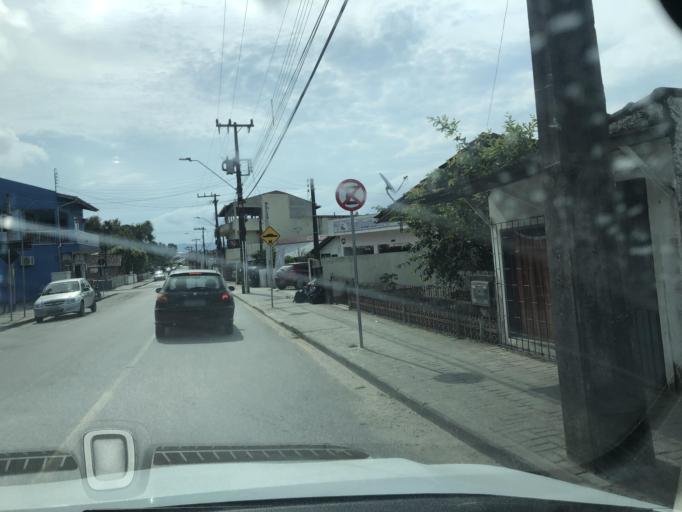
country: BR
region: Santa Catarina
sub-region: Sao Francisco Do Sul
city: Sao Francisco do Sul
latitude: -26.2302
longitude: -48.6126
